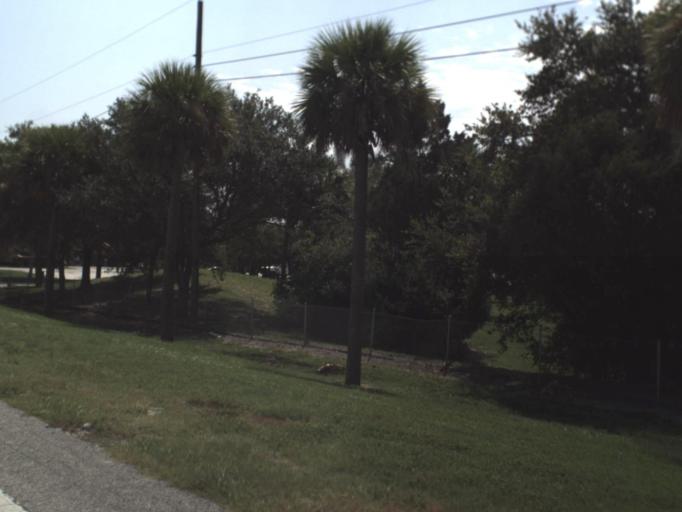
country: US
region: Florida
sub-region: Pinellas County
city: Gandy
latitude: 27.8909
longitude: -82.5407
